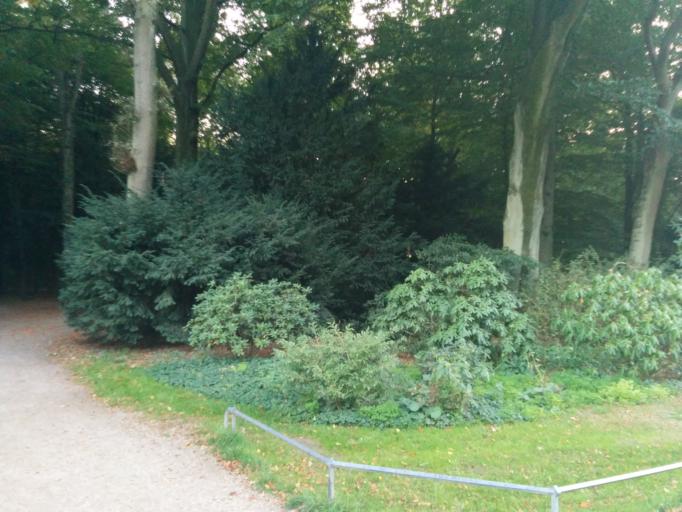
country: DE
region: Hamburg
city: Winterhude
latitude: 53.5967
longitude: 10.0113
